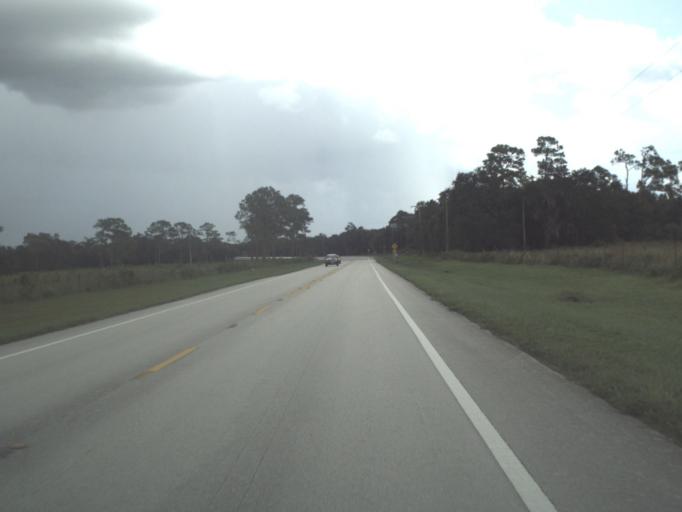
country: US
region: Florida
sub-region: DeSoto County
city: Nocatee
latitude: 27.2015
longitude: -81.9944
